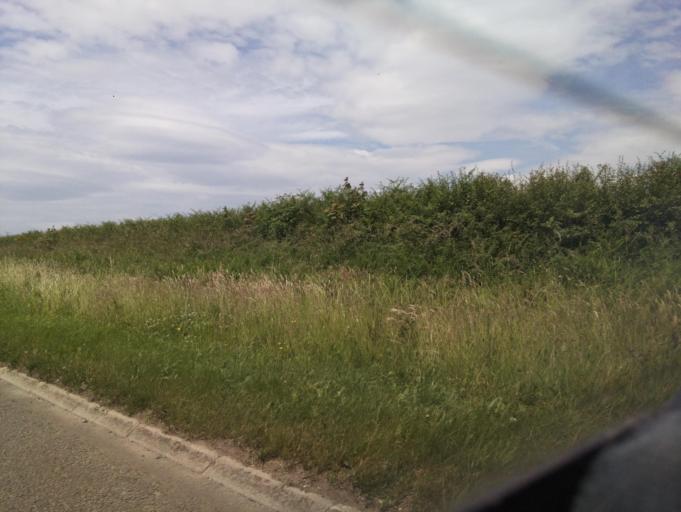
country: GB
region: Wales
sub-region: Vale of Glamorgan
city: Llangan
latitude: 51.4752
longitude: -3.5054
